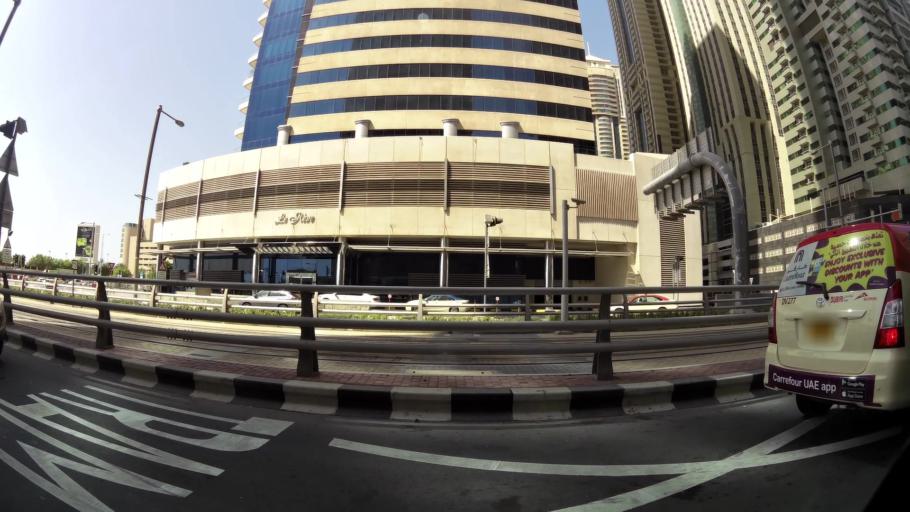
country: AE
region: Dubai
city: Dubai
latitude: 25.0888
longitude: 55.1473
